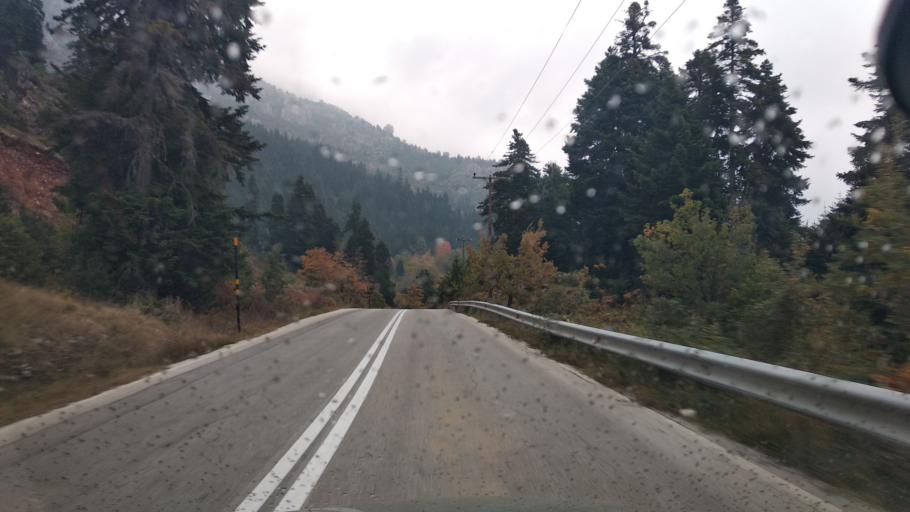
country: GR
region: Thessaly
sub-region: Trikala
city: Pyli
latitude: 39.5228
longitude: 21.5195
